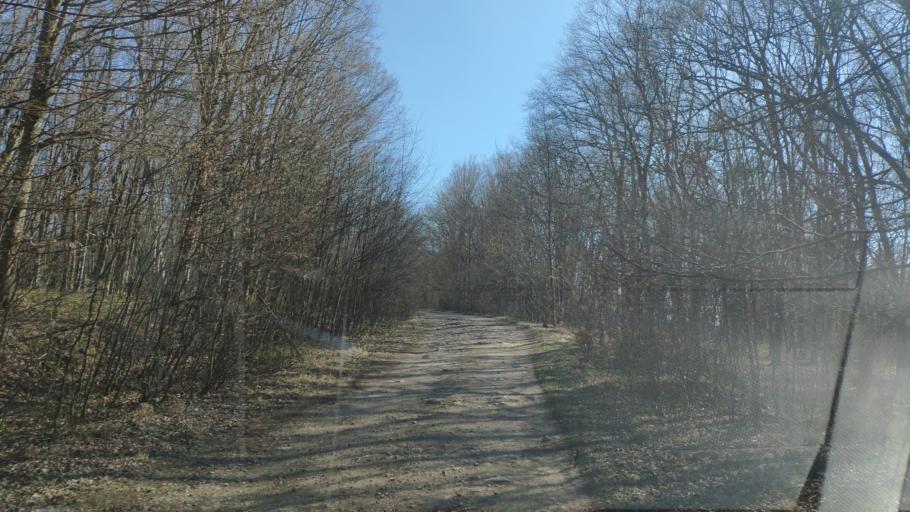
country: SK
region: Kosicky
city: Roznava
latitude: 48.5986
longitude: 20.4108
